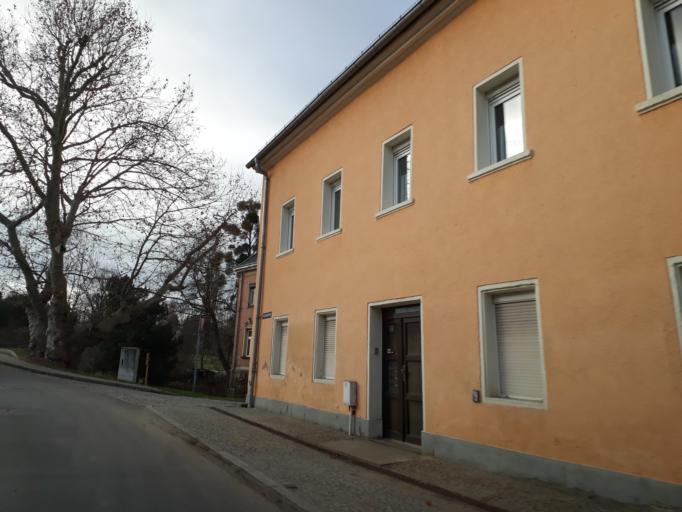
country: DE
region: Saxony
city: Weissenberg
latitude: 51.1956
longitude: 14.6563
